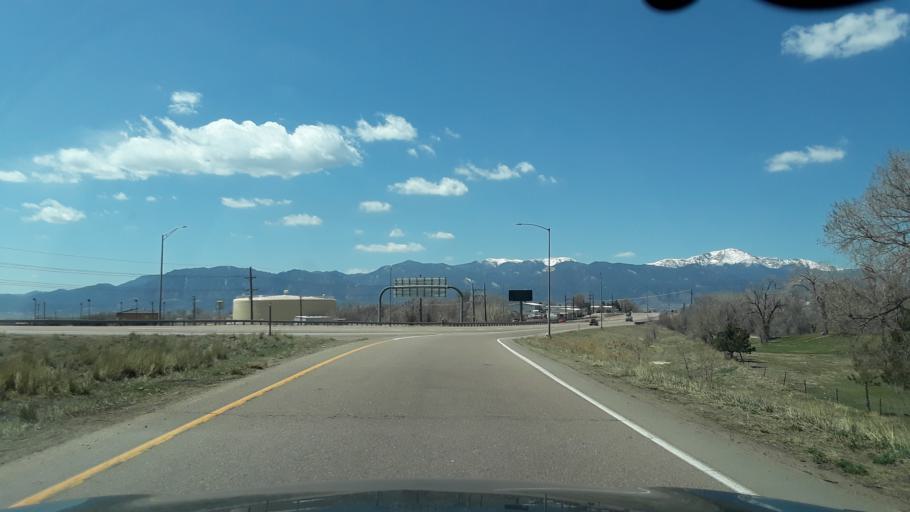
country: US
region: Colorado
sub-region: El Paso County
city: Cimarron Hills
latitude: 38.8395
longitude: -104.7035
